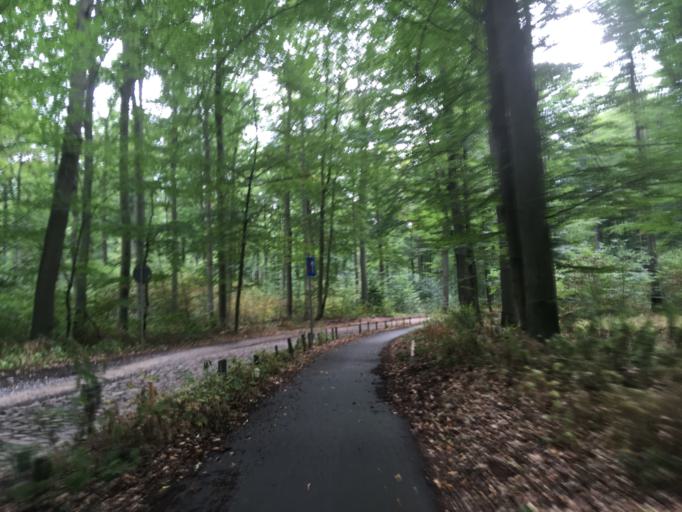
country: DE
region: Brandenburg
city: Chorin
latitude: 52.9178
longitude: 13.8577
